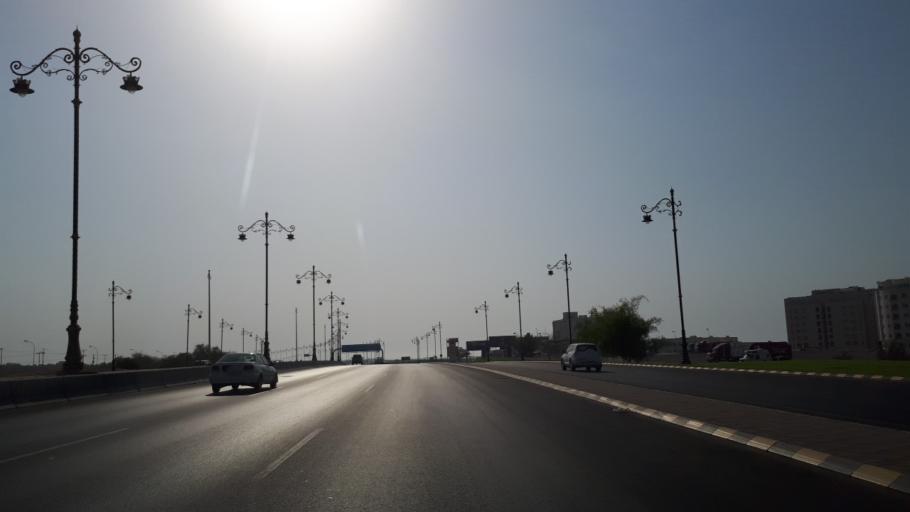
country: OM
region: Muhafazat Masqat
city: Bawshar
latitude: 23.5909
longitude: 58.3520
